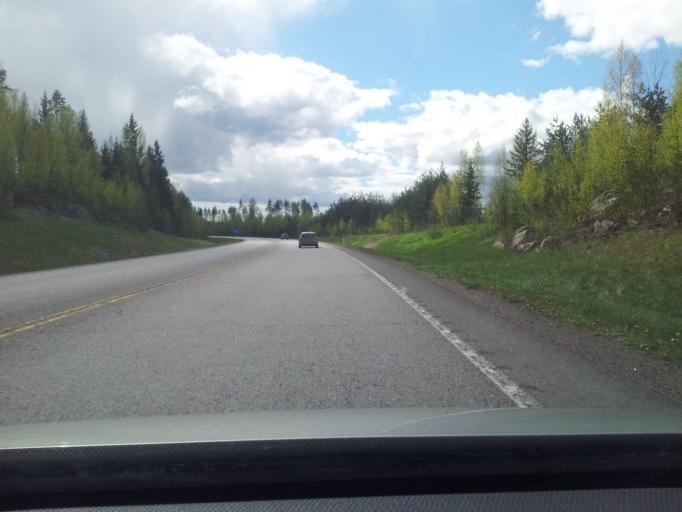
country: FI
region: Uusimaa
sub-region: Loviisa
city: Perna
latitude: 60.5209
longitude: 25.9633
